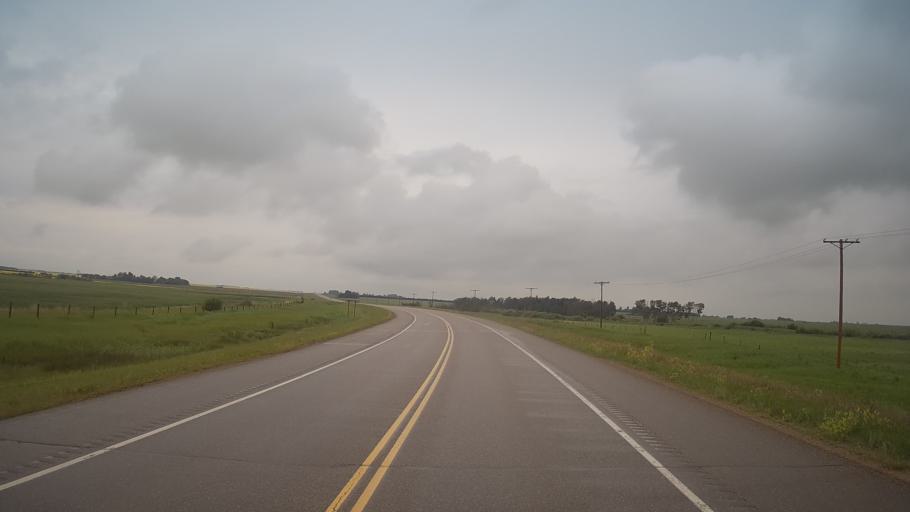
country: CA
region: Saskatchewan
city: Wilkie
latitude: 52.4346
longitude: -108.9316
